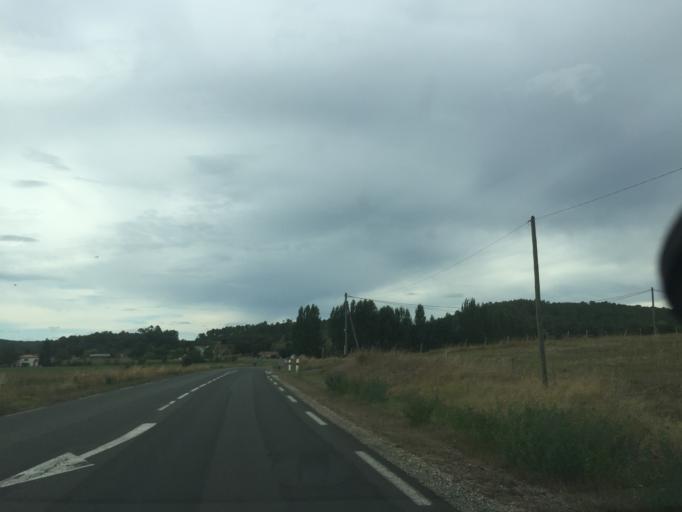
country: FR
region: Aquitaine
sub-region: Departement du Lot-et-Garonne
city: Fumel
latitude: 44.5164
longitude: 0.9474
